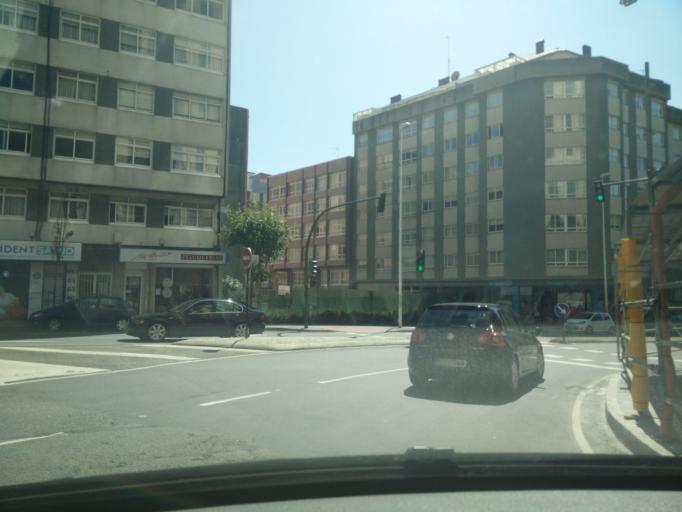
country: ES
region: Galicia
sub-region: Provincia da Coruna
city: A Coruna
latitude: 43.3739
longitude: -8.4249
